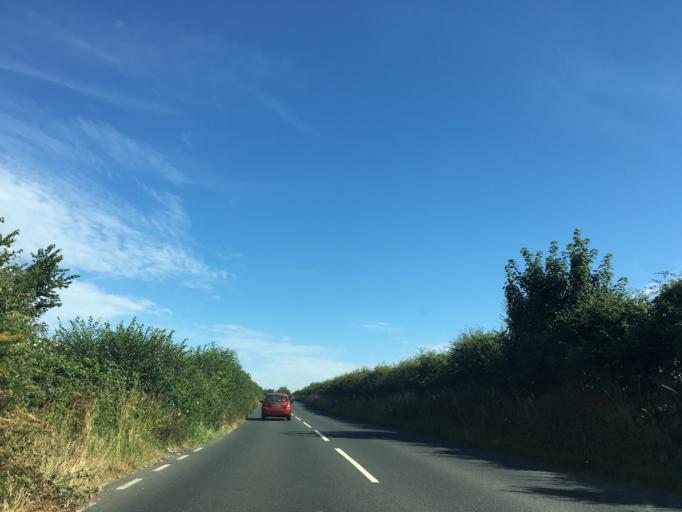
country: GB
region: England
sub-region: Isle of Wight
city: Newport
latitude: 50.6752
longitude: -1.3041
